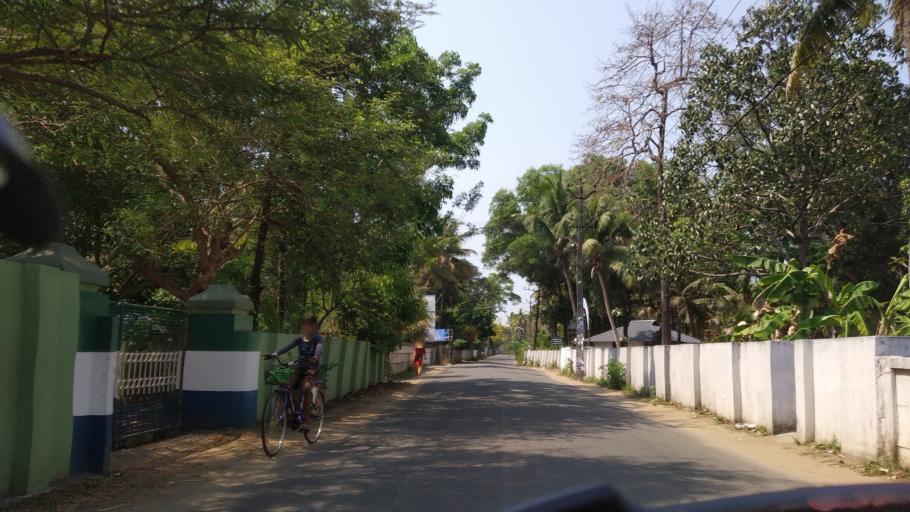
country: IN
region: Kerala
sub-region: Thrissur District
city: Kodungallur
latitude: 10.2497
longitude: 76.1485
